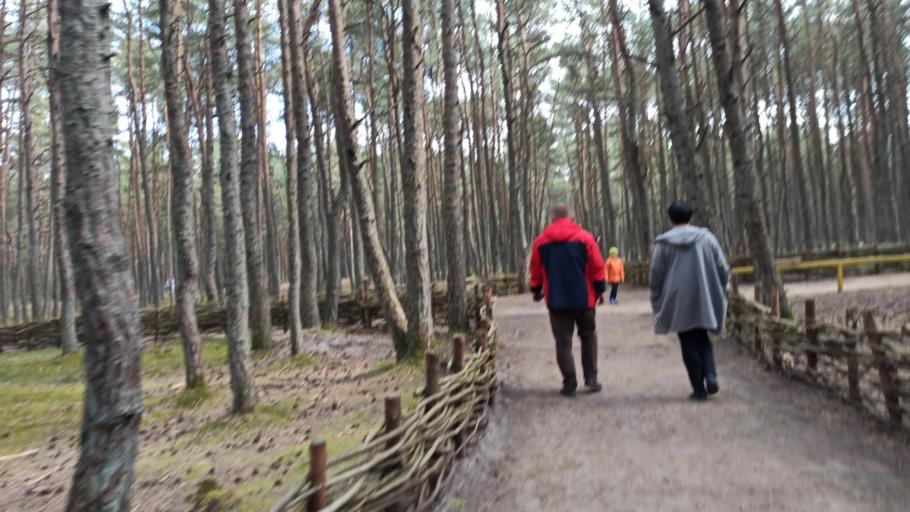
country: LT
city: Nida
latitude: 55.1813
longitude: 20.8626
